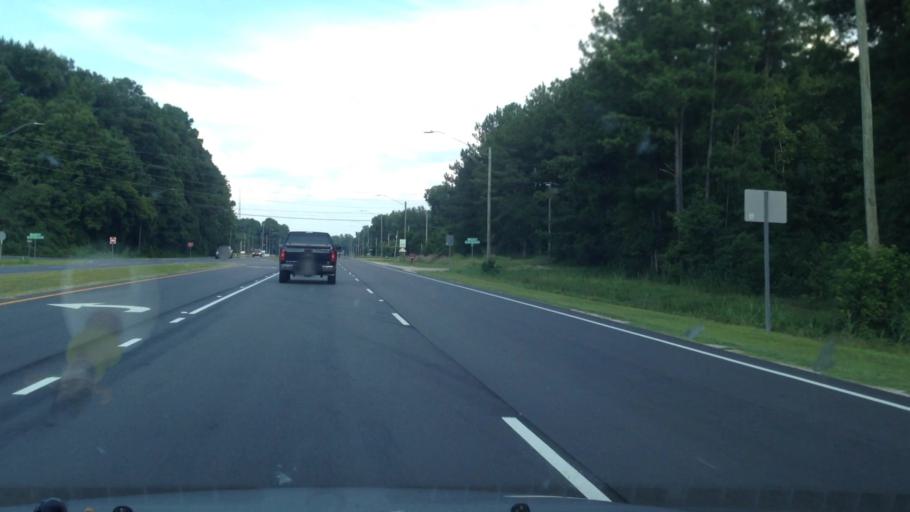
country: US
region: North Carolina
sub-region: Harnett County
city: Buies Creek
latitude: 35.4093
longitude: -78.7759
